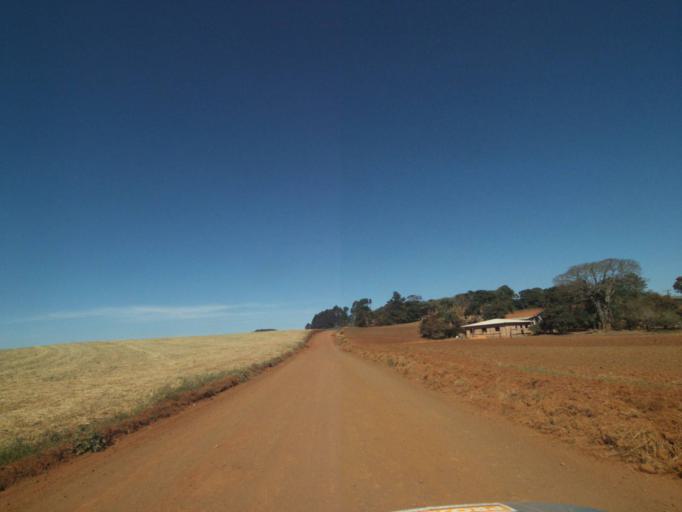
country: BR
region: Parana
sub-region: Tibagi
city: Tibagi
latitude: -24.5820
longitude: -50.6116
